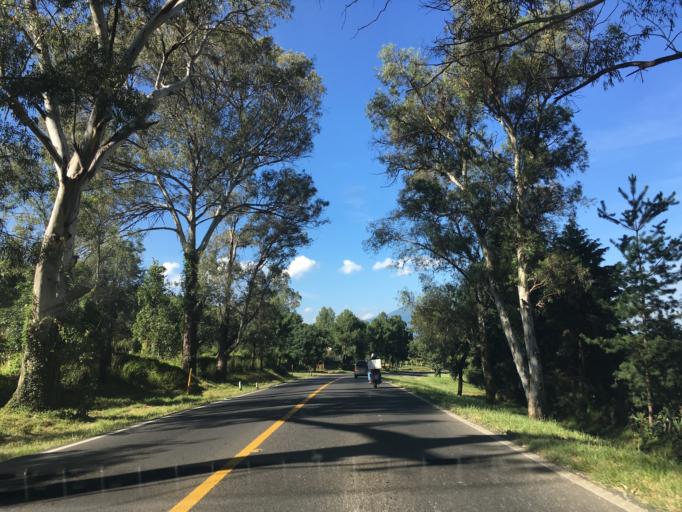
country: MX
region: Michoacan
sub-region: Chilchota
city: Ichan
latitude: 19.8488
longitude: -102.0584
